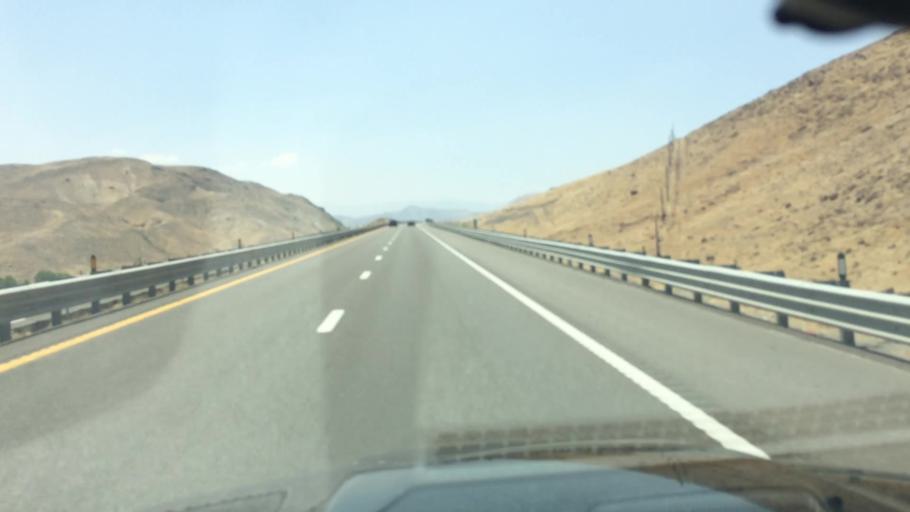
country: US
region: Nevada
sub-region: Washoe County
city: Spanish Springs
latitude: 39.5527
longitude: -119.5690
